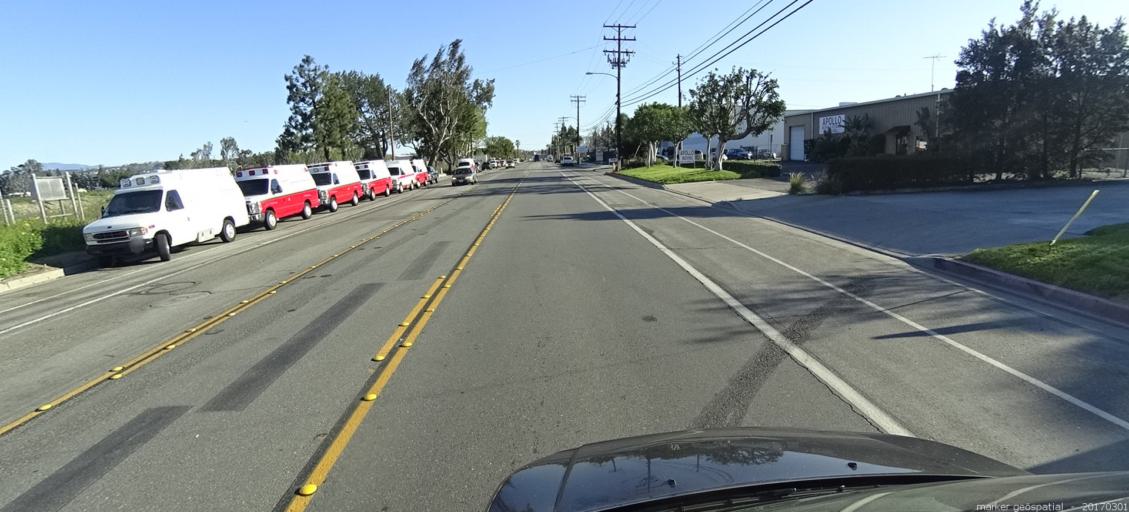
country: US
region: California
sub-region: Orange County
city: Placentia
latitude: 33.8643
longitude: -117.8508
